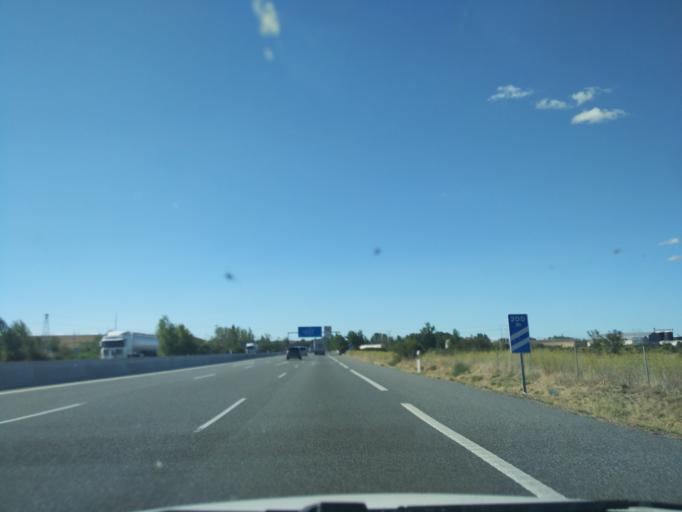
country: ES
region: Castille and Leon
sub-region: Provincia de Zamora
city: Benavente
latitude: 42.0103
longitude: -5.6630
